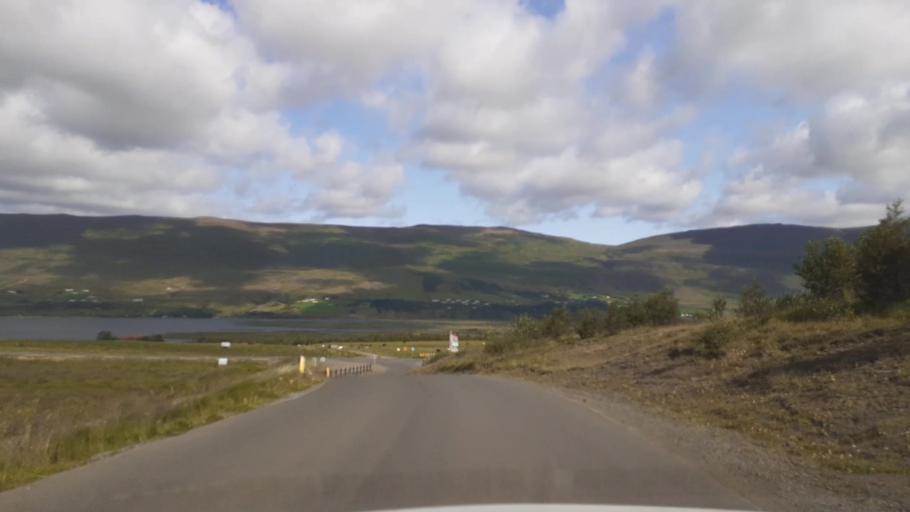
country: IS
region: Northeast
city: Akureyri
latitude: 65.6512
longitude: -18.0955
